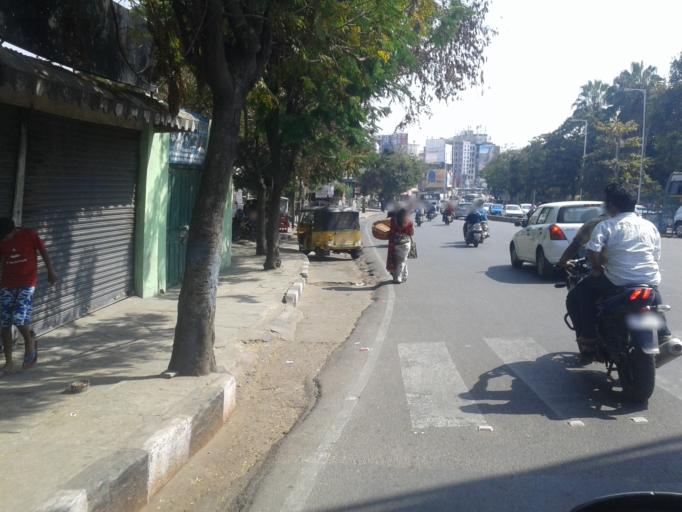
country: IN
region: Telangana
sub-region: Hyderabad
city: Hyderabad
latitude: 17.4088
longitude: 78.4757
